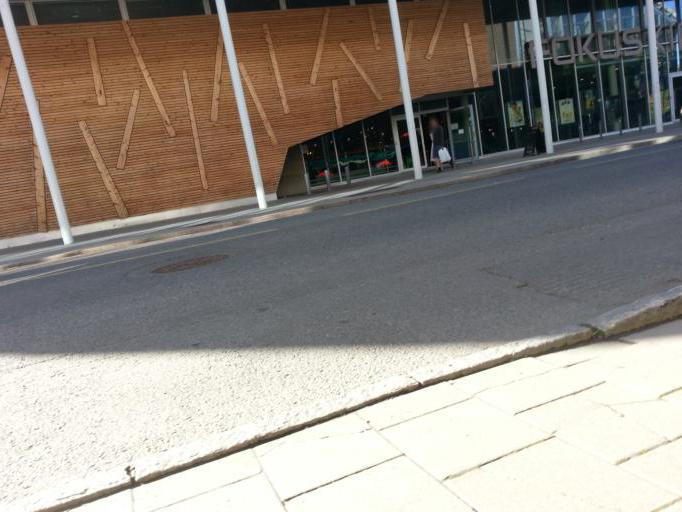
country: NO
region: Troms
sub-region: Tromso
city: Tromso
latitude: 69.6510
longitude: 18.9559
